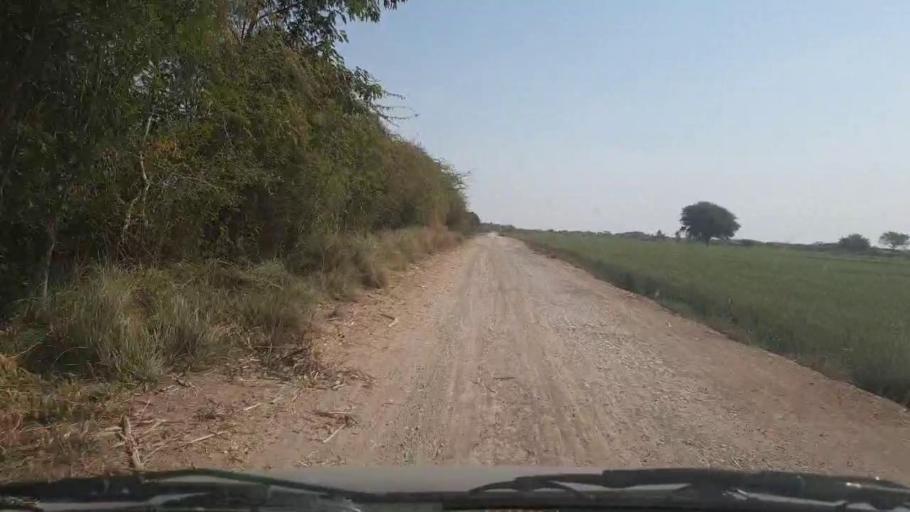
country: PK
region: Sindh
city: Samaro
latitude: 25.2216
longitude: 69.3348
